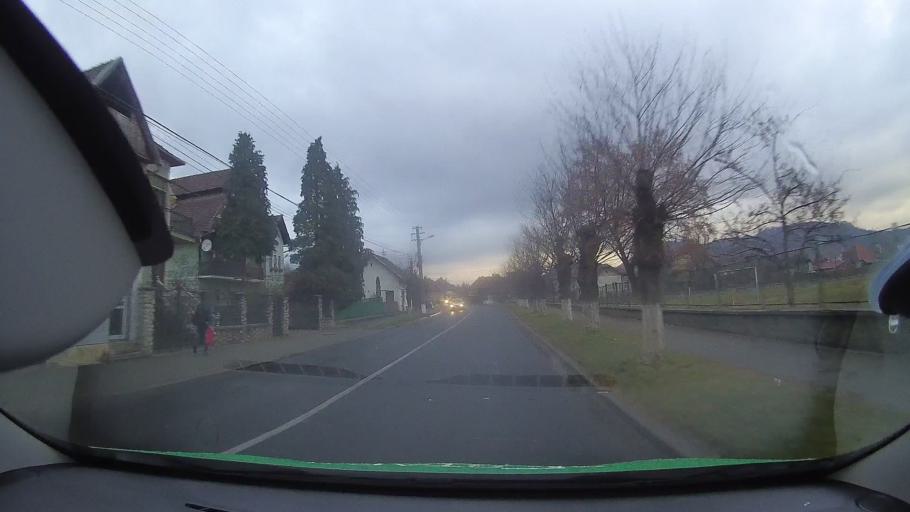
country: RO
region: Hunedoara
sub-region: Municipiul Brad
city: Brad
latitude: 46.1312
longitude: 22.7840
